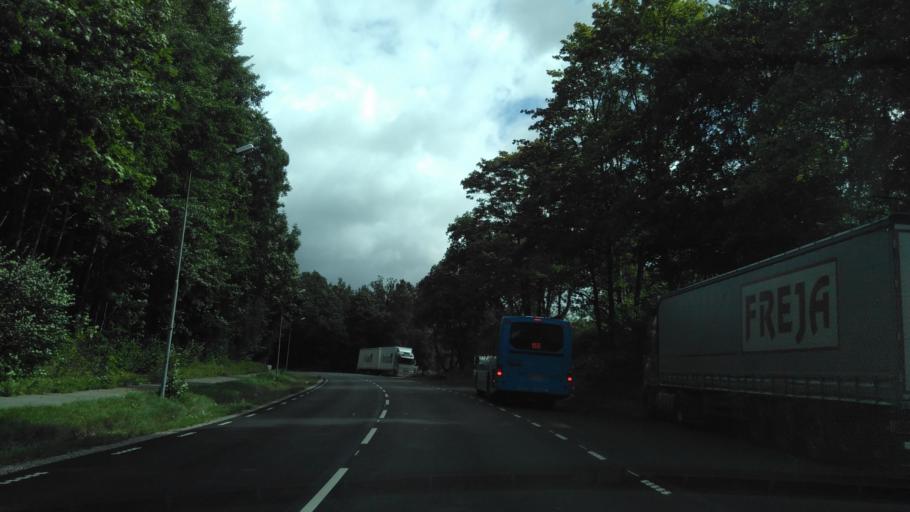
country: SE
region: Vaestra Goetaland
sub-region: Boras Kommun
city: Viskafors
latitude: 57.6193
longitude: 12.8211
